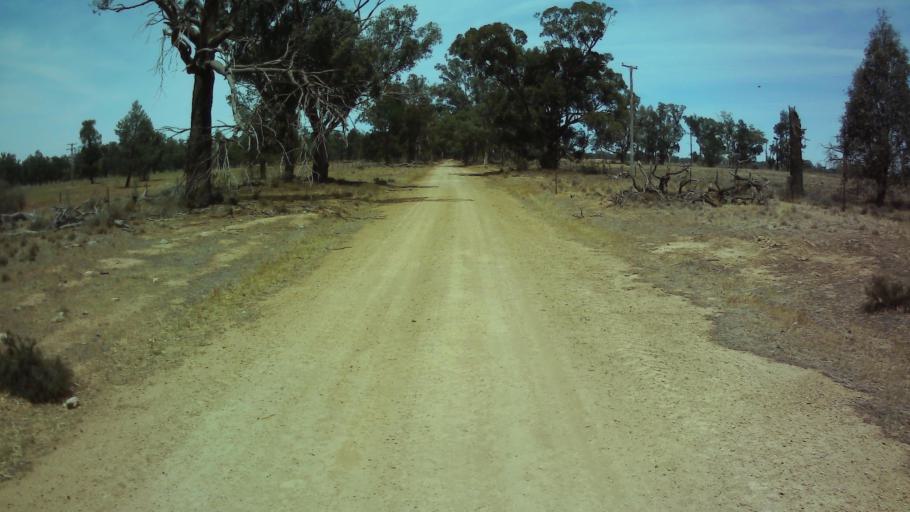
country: AU
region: New South Wales
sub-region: Weddin
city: Grenfell
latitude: -34.0291
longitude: 147.9387
